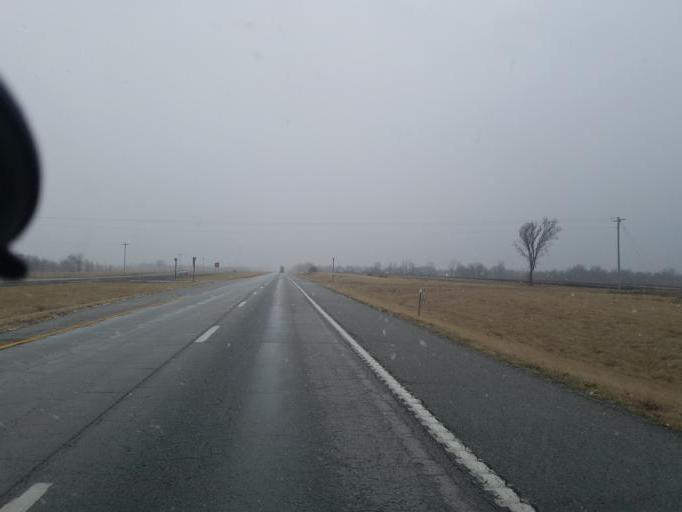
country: US
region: Missouri
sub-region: Macon County
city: La Plata
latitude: 39.9341
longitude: -92.4766
